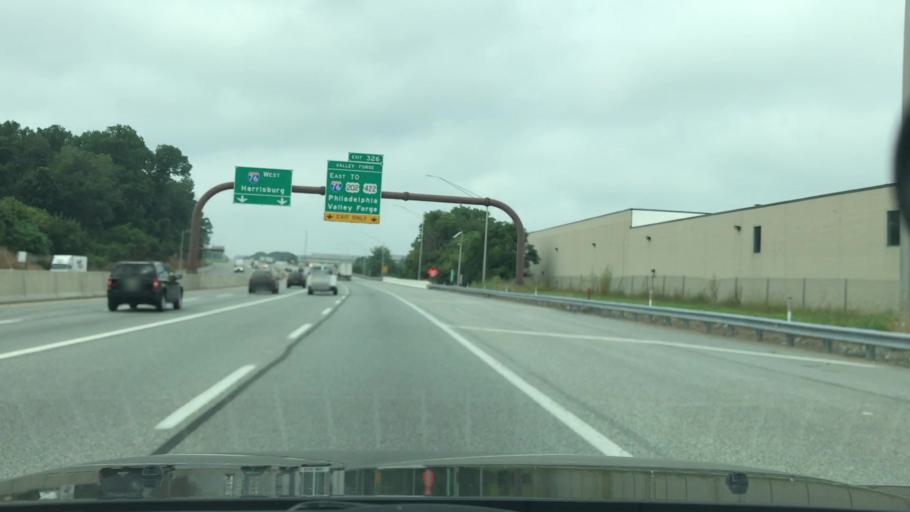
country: US
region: Pennsylvania
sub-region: Montgomery County
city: King of Prussia
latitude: 40.0935
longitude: -75.4014
